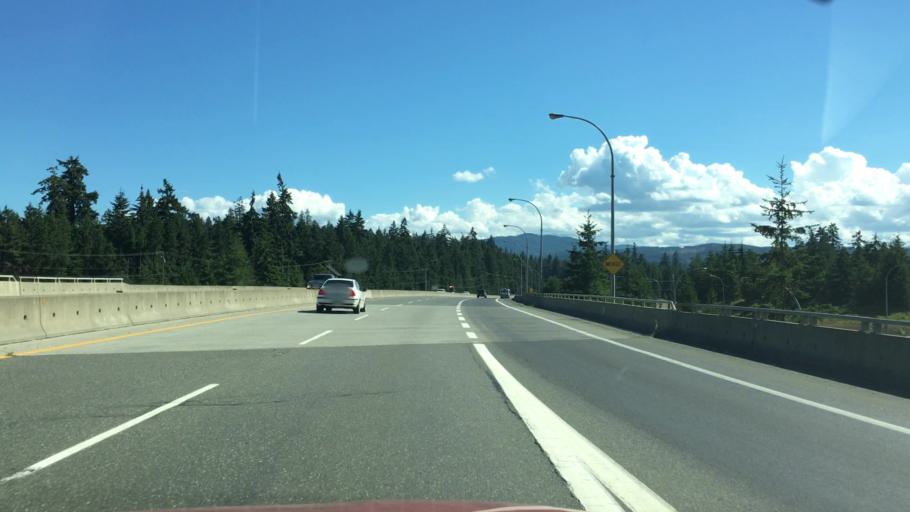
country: CA
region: British Columbia
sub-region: Regional District of Nanaimo
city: Parksville
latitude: 49.2983
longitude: -124.2560
